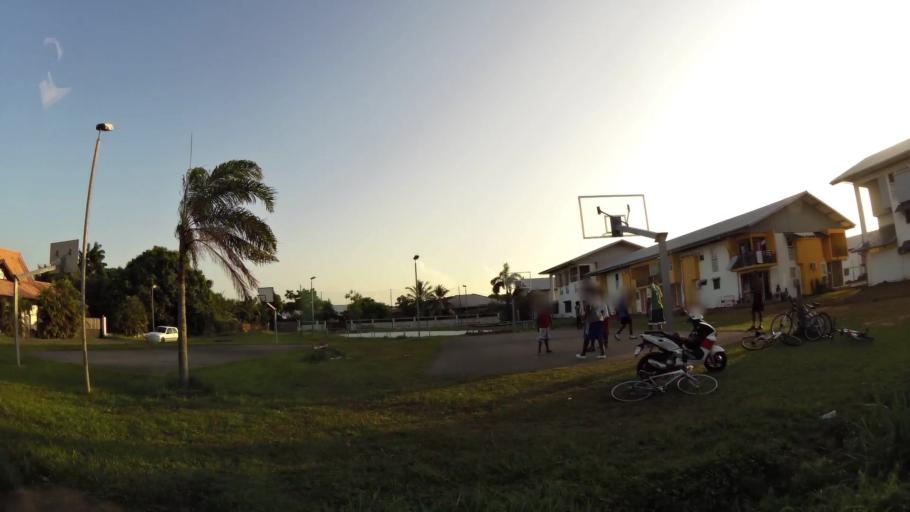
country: GF
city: Macouria
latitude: 5.0092
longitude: -52.4702
